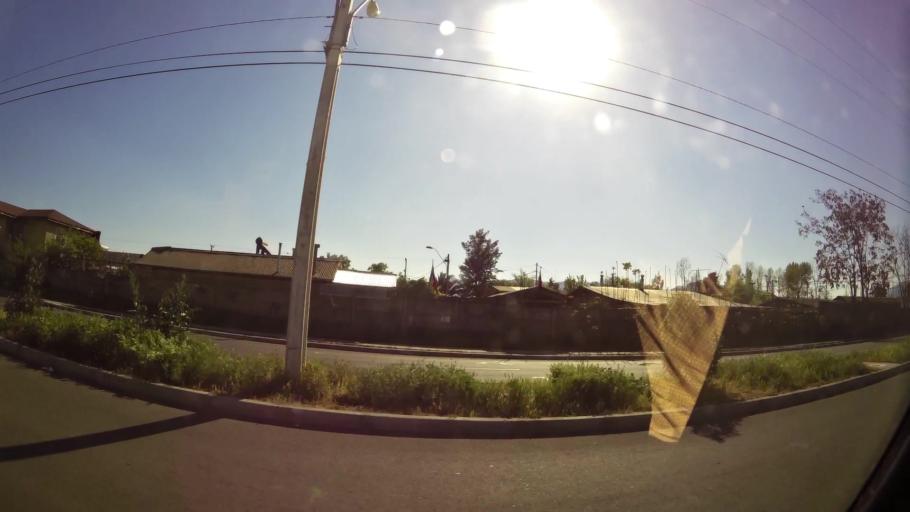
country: CL
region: Santiago Metropolitan
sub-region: Provincia de Talagante
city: Penaflor
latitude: -33.6117
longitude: -70.8804
